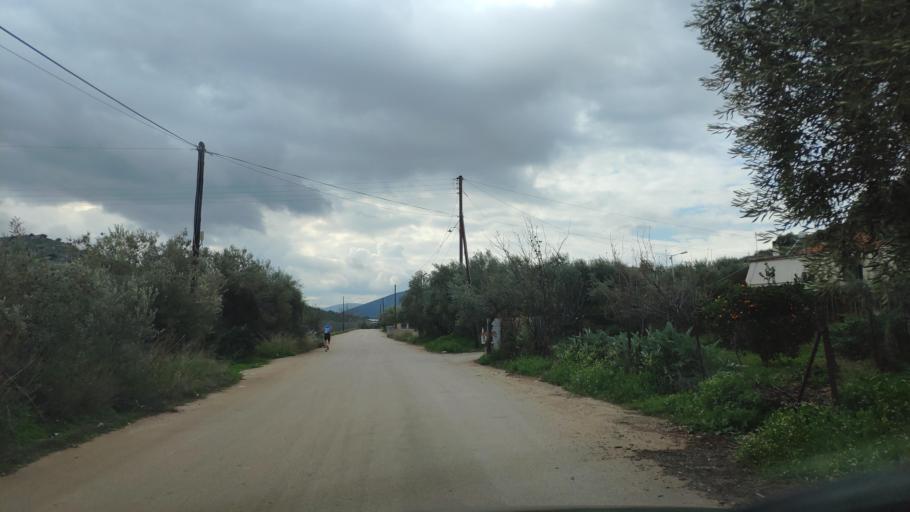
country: GR
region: Peloponnese
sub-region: Nomos Argolidos
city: Nea Kios
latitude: 37.5444
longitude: 22.7119
